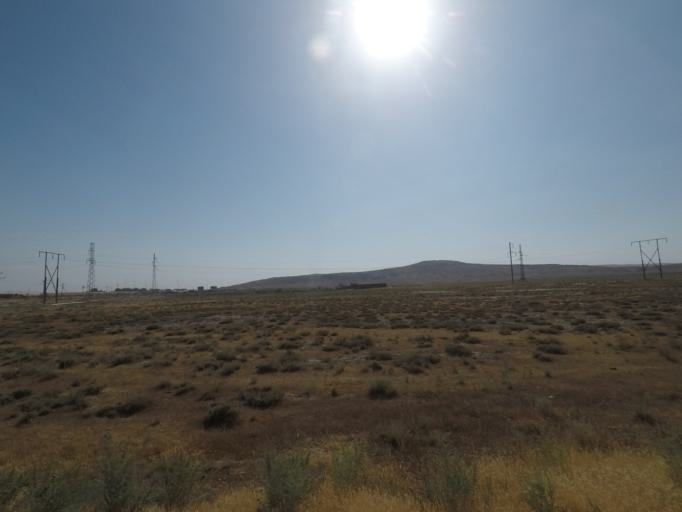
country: AZ
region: Baki
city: Qobustan
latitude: 39.9714
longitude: 49.3954
